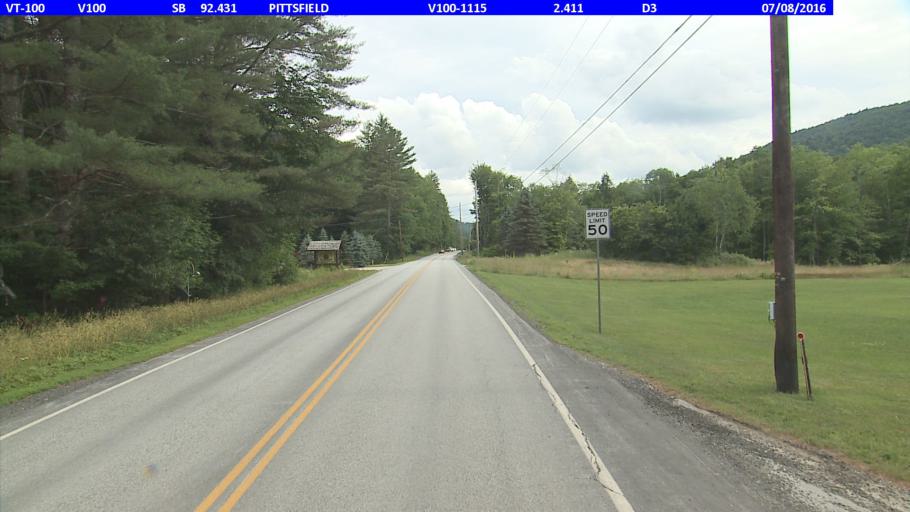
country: US
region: Vermont
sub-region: Rutland County
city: Rutland
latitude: 43.7518
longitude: -72.8208
